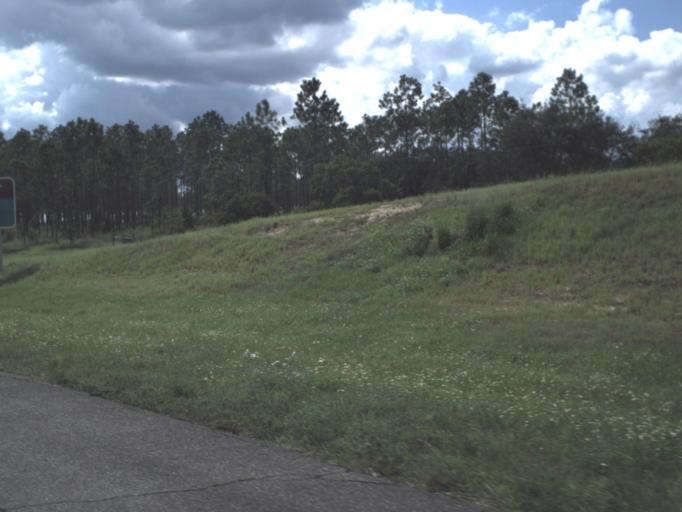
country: US
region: Florida
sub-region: Polk County
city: Loughman
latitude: 28.2438
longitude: -81.6350
